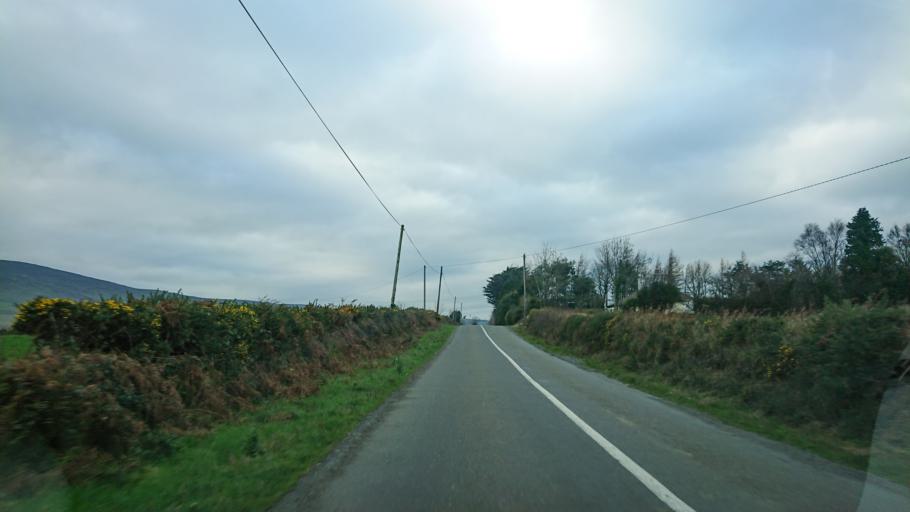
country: IE
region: Munster
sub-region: South Tipperary
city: Cluain Meala
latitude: 52.3204
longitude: -7.5617
